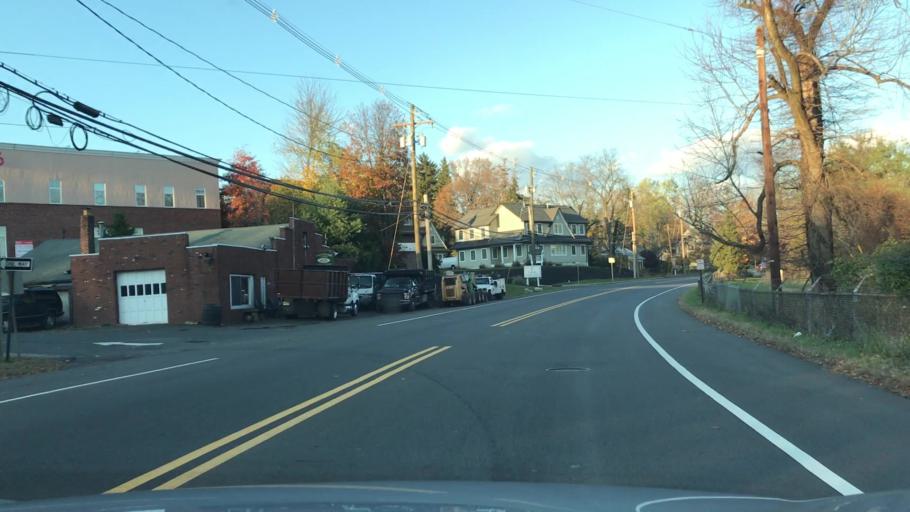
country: US
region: New Jersey
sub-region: Bergen County
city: Harrington Park
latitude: 40.9818
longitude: -73.9784
